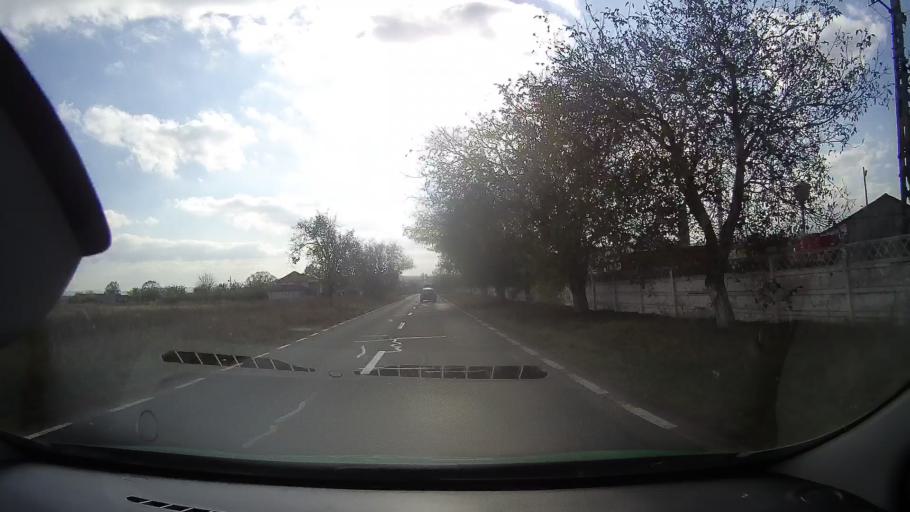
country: RO
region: Tulcea
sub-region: Comuna Nalbant
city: Nalbant
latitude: 45.0536
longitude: 28.6183
